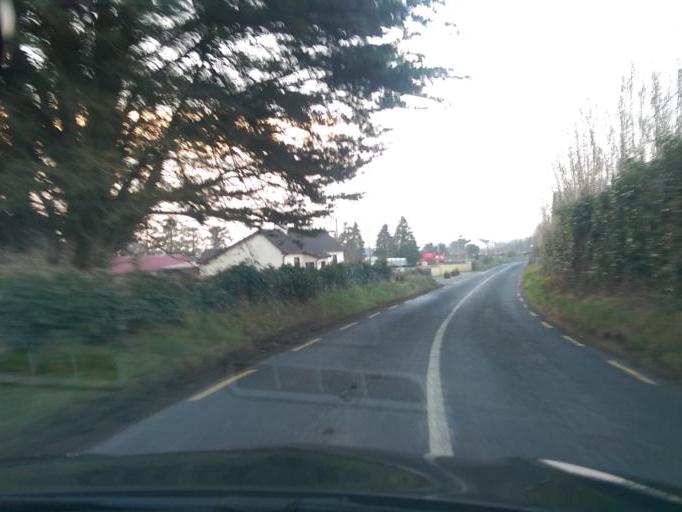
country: IE
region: Connaught
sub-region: County Galway
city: Loughrea
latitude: 53.2306
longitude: -8.6452
